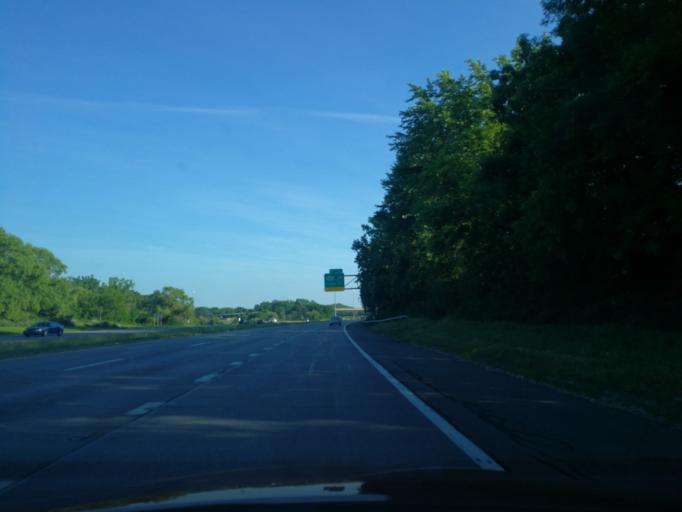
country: US
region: New York
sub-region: Monroe County
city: Greece
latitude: 43.2125
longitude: -77.6750
